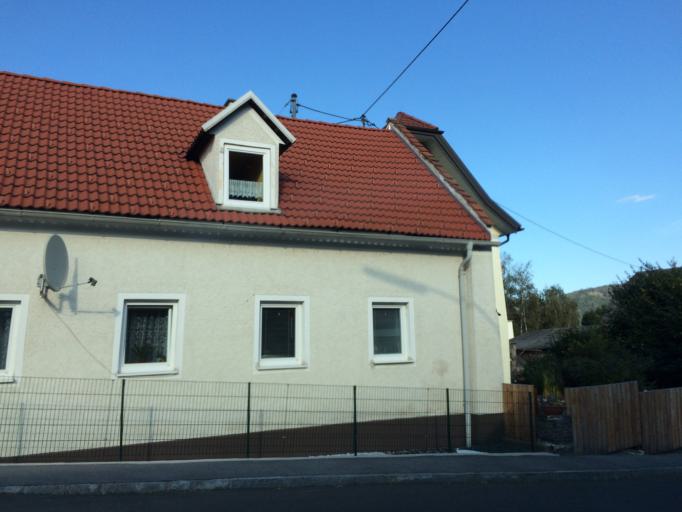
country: AT
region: Styria
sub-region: Politischer Bezirk Leoben
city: Kraubath an der Mur
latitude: 47.3056
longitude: 14.9374
